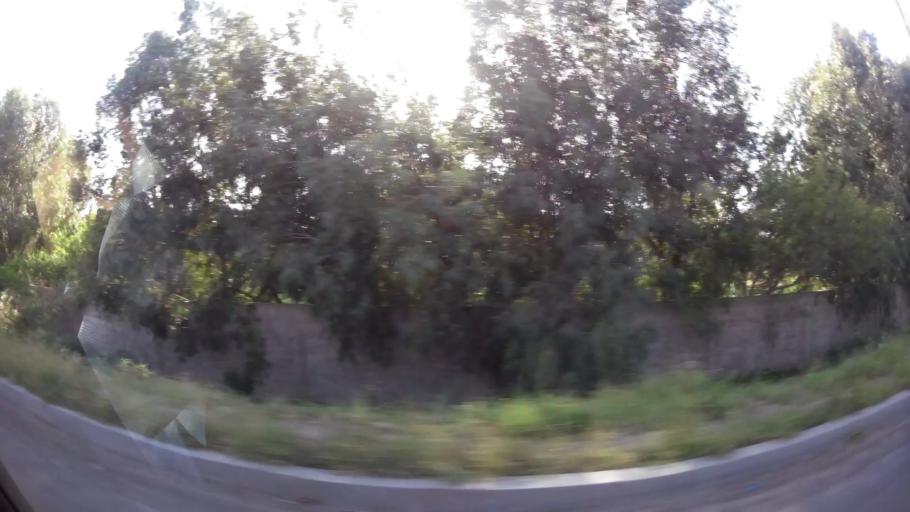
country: MA
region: Souss-Massa-Draa
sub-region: Inezgane-Ait Mellou
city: Inezgane
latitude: 30.3568
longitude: -9.5060
